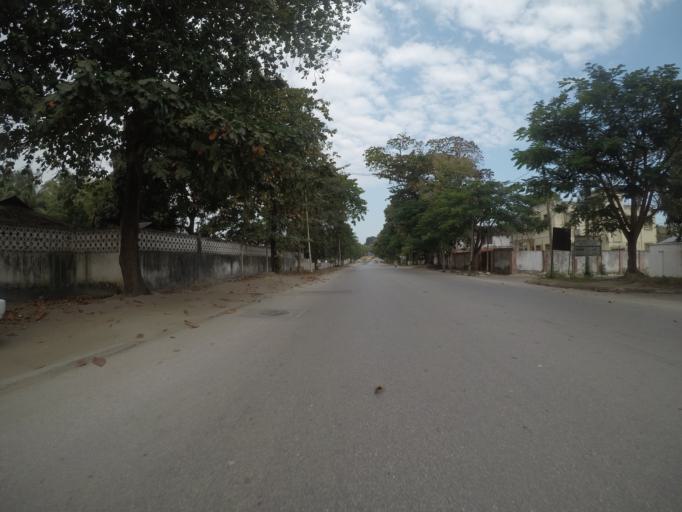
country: TZ
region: Zanzibar Urban/West
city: Zanzibar
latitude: -6.1743
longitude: 39.1996
